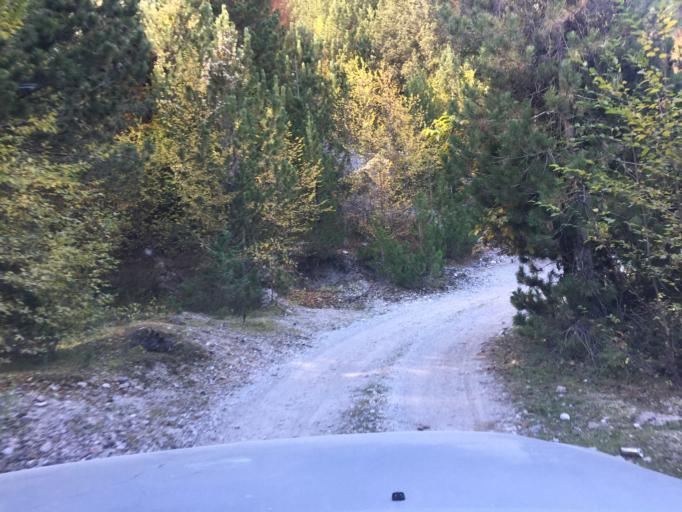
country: AL
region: Shkoder
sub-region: Rrethi i Shkodres
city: Nicaj-Shale
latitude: 42.3896
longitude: 19.7772
